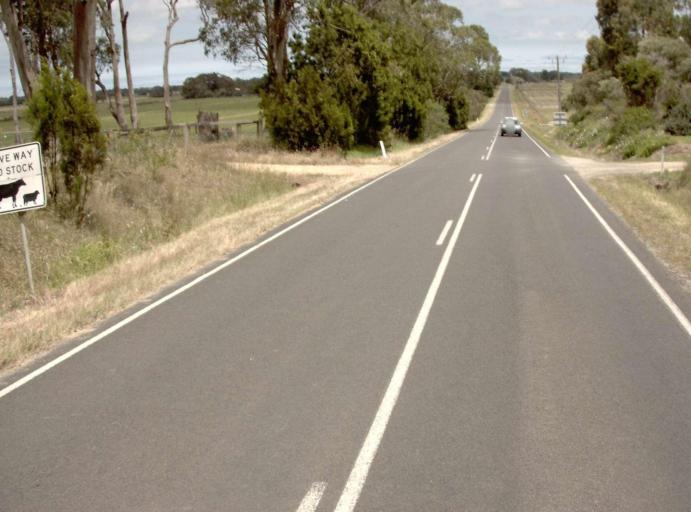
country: AU
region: Victoria
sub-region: Latrobe
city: Traralgon
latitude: -38.5418
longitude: 146.6564
